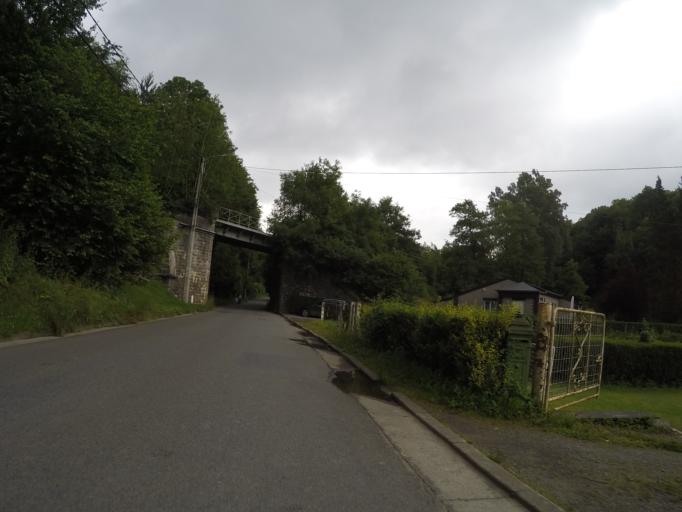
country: BE
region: Wallonia
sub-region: Province de Namur
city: Yvoir
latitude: 50.3334
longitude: 4.8978
